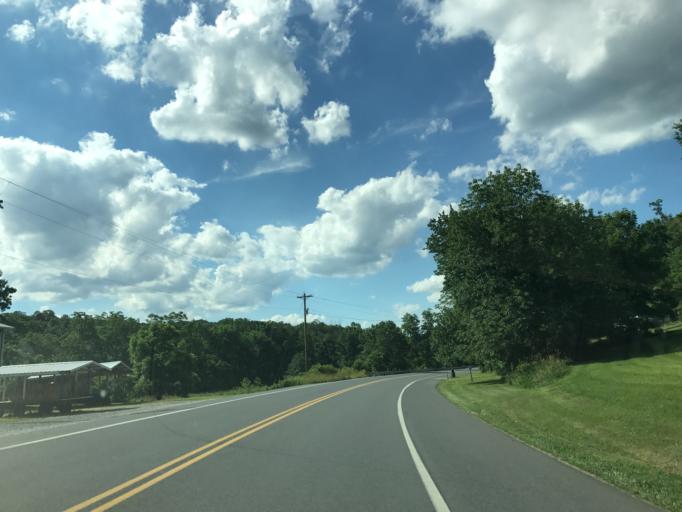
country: US
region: Pennsylvania
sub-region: York County
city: Parkville
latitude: 39.7671
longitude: -76.8776
